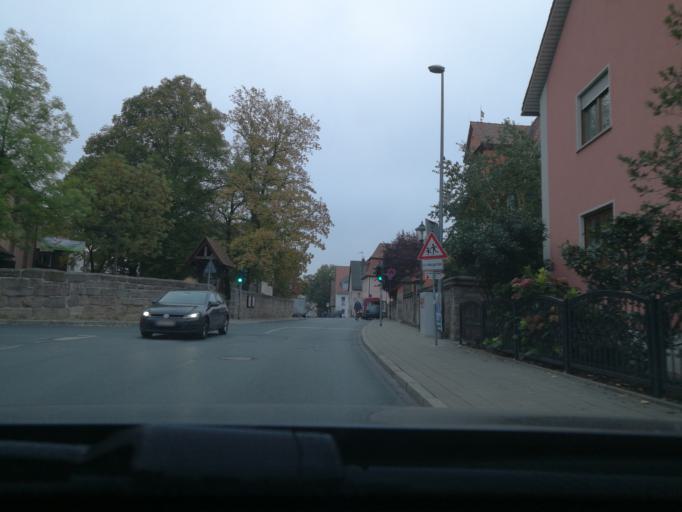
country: DE
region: Bavaria
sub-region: Regierungsbezirk Mittelfranken
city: Furth
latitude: 49.4820
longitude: 11.0144
